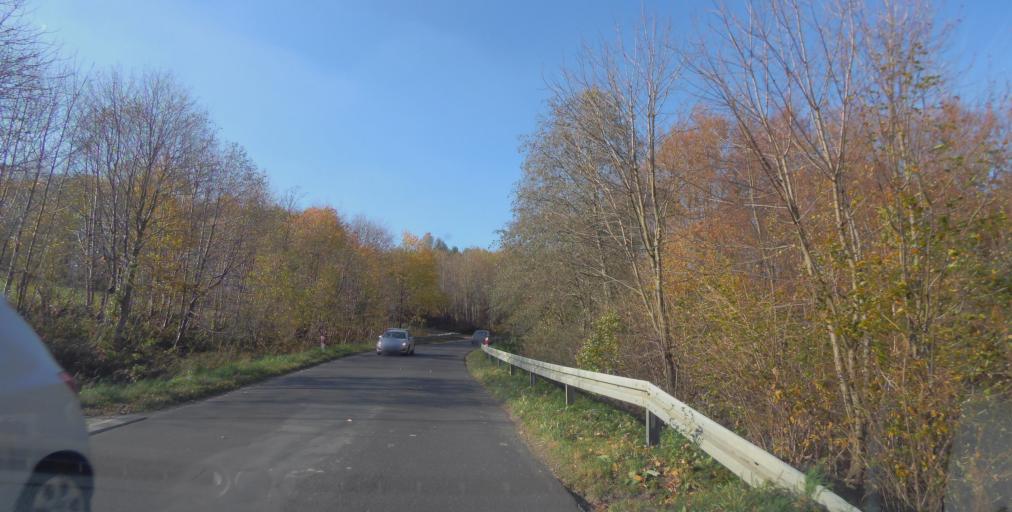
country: PL
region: Subcarpathian Voivodeship
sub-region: Powiat leski
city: Polanczyk
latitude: 49.3439
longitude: 22.4132
